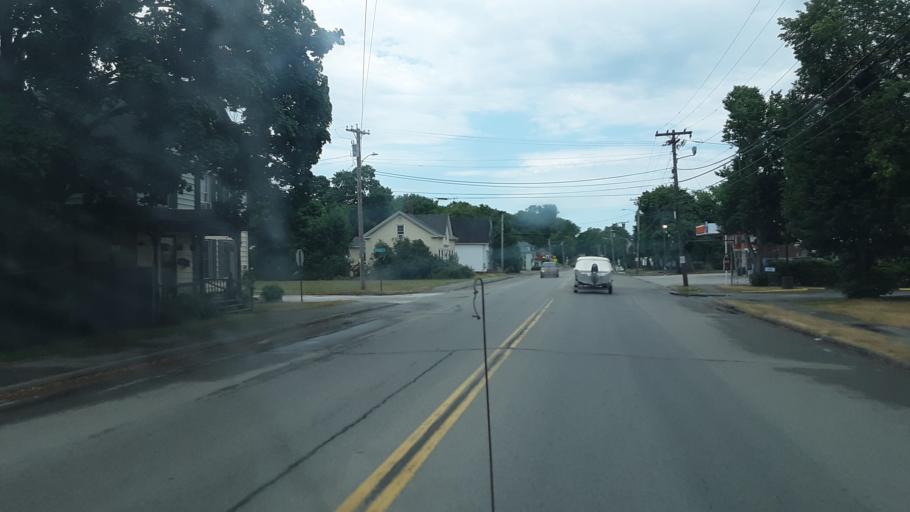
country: US
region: Maine
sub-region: Penobscot County
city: Brewer
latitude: 44.7927
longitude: -68.7676
